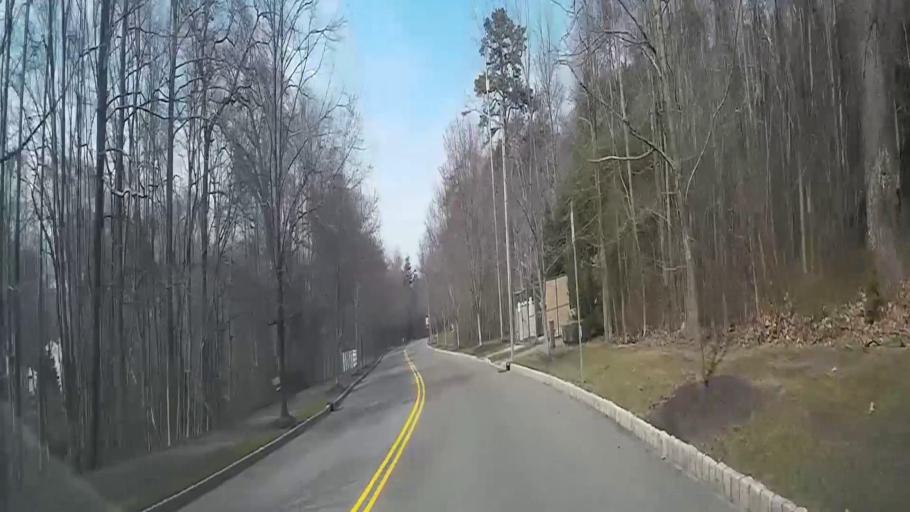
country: US
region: New Jersey
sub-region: Burlington County
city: Marlton
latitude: 39.8673
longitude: -74.8665
